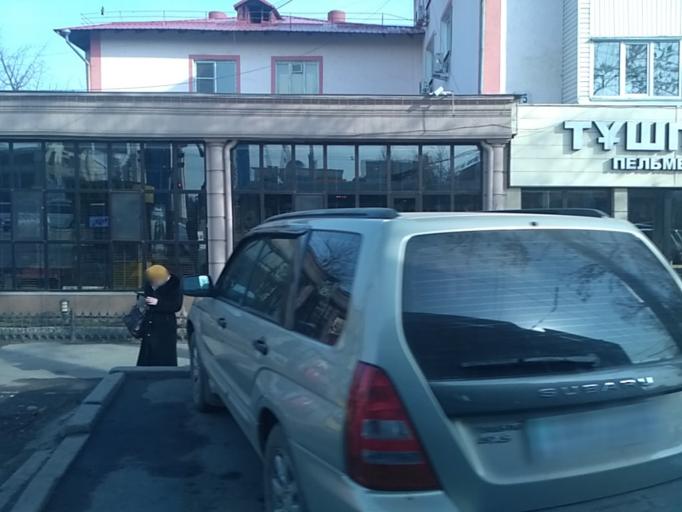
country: KZ
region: Almaty Qalasy
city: Almaty
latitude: 43.2260
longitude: 76.9063
